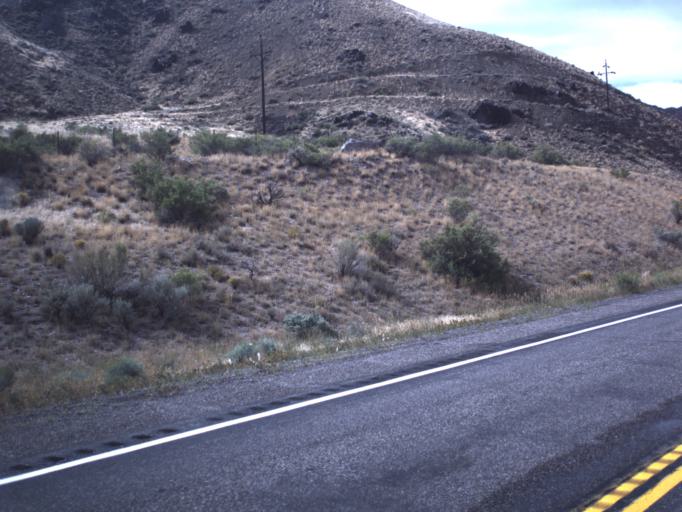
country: US
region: Utah
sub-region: Sevier County
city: Monroe
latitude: 38.4933
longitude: -112.2489
